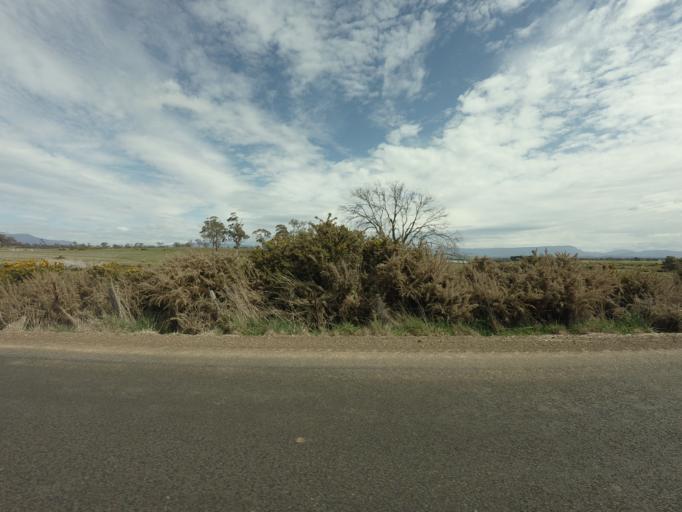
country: AU
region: Tasmania
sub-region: Northern Midlands
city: Longford
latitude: -41.7216
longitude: 147.1889
